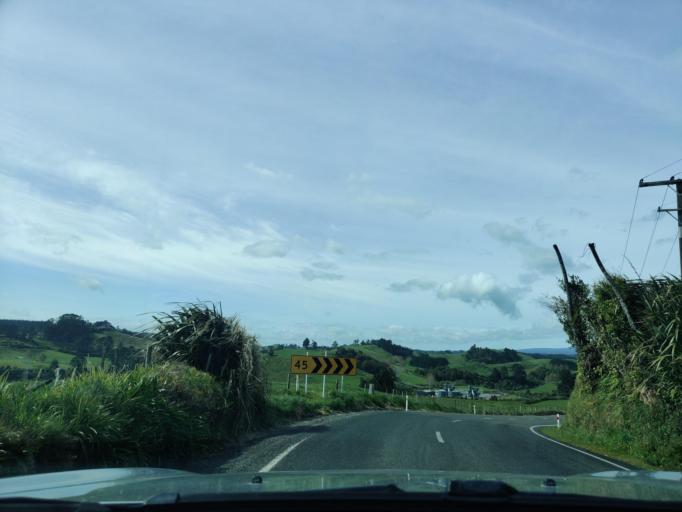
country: NZ
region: Taranaki
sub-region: New Plymouth District
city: New Plymouth
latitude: -39.1098
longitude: 174.1014
